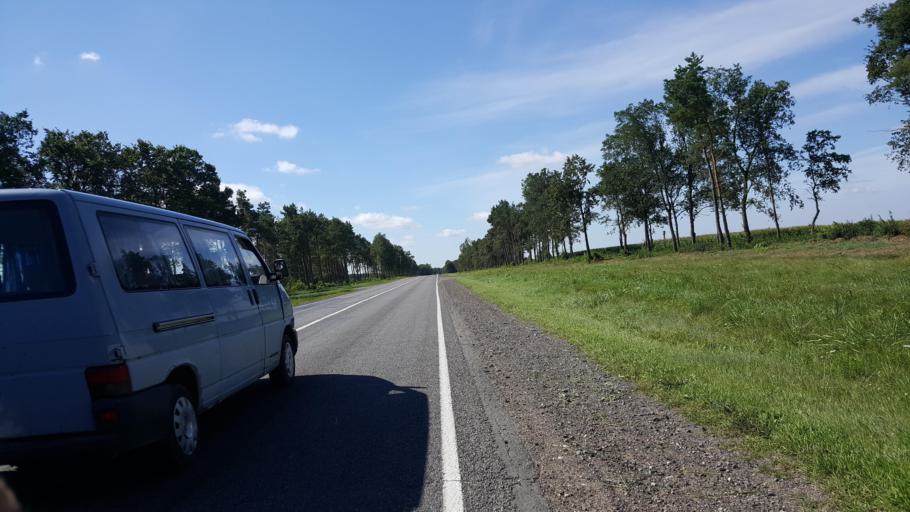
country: BY
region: Brest
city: Charnawchytsy
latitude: 52.2833
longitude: 23.7726
